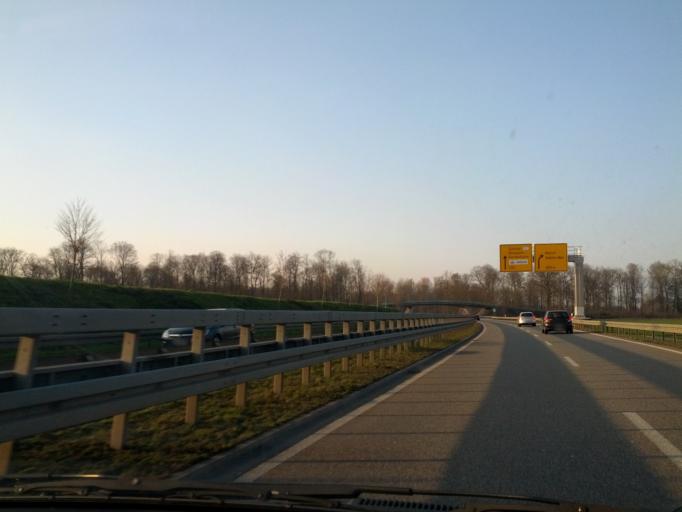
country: DE
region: Baden-Wuerttemberg
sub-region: Freiburg Region
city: Umkirch
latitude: 48.0326
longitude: 7.7789
